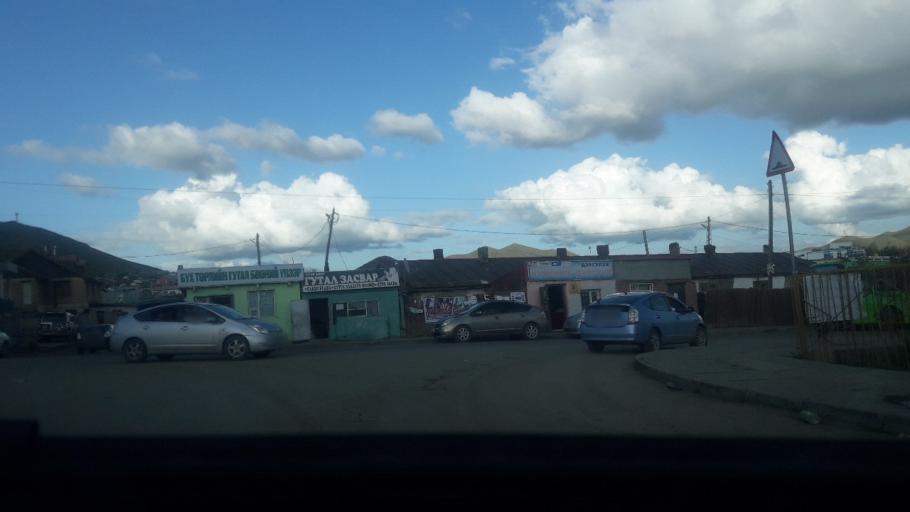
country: MN
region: Ulaanbaatar
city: Ulaanbaatar
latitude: 47.9345
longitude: 107.0057
